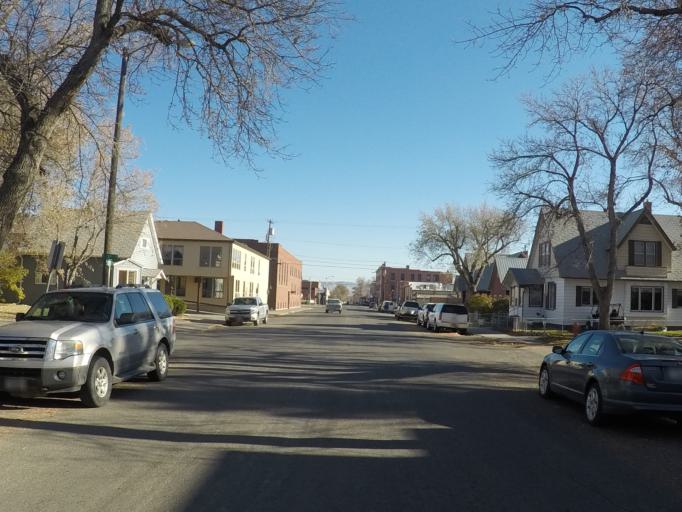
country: US
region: Montana
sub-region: Park County
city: Livingston
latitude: 45.6590
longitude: -110.5614
